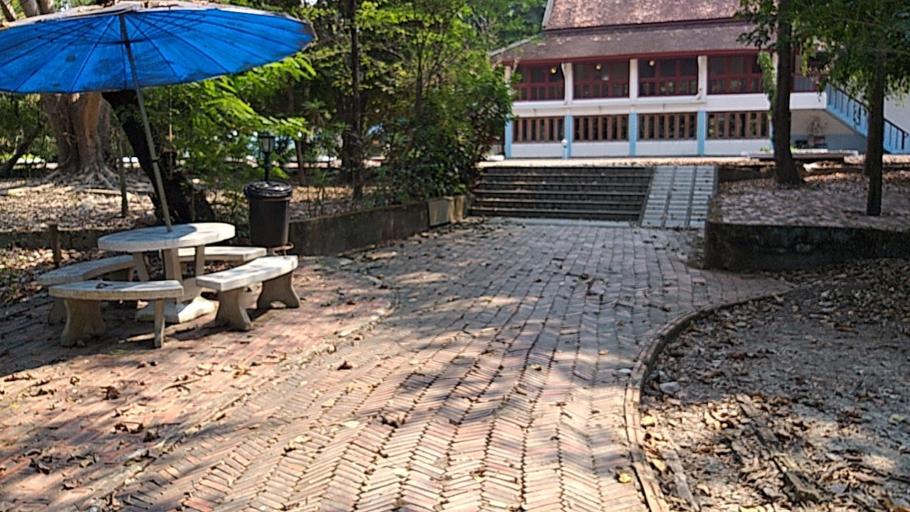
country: TH
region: Nakhon Nayok
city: Ongkharak
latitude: 14.1260
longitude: 100.9443
